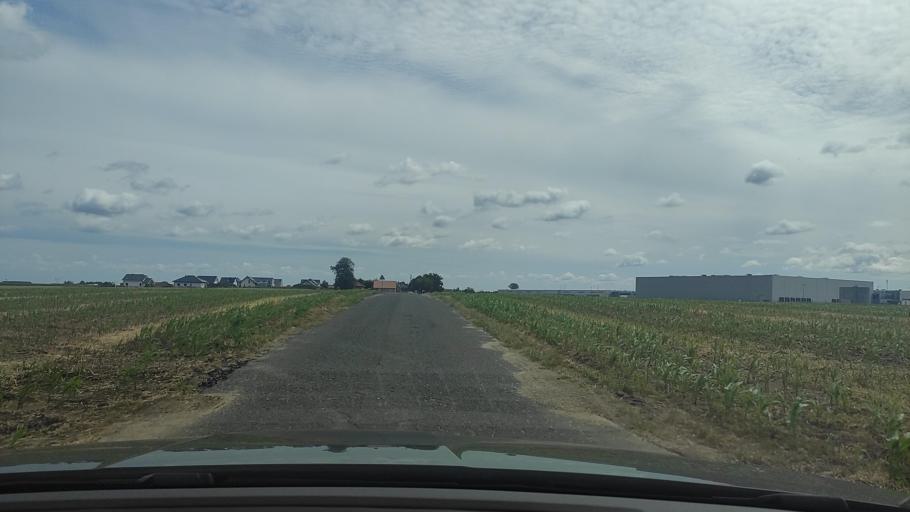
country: PL
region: Greater Poland Voivodeship
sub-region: Powiat poznanski
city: Kostrzyn
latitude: 52.4066
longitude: 17.1975
